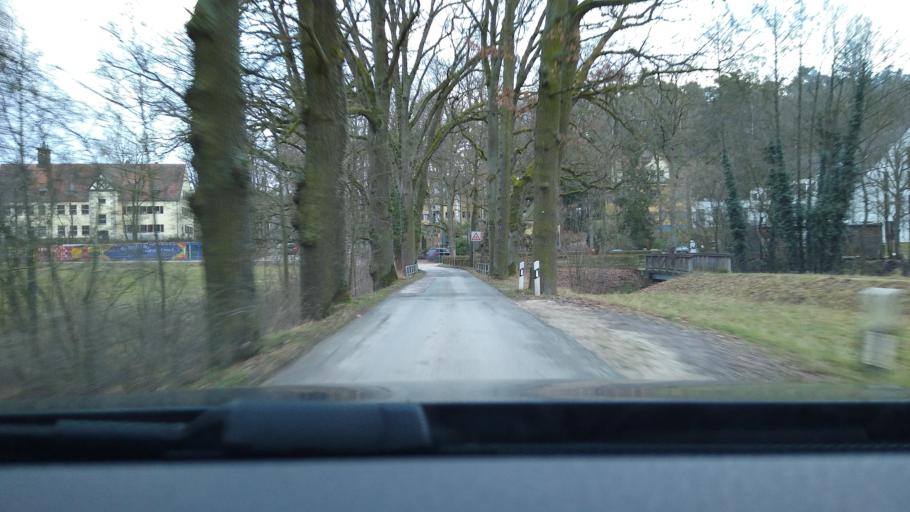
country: DE
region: Bavaria
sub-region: Regierungsbezirk Mittelfranken
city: Schwabach
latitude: 49.3630
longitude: 11.0149
